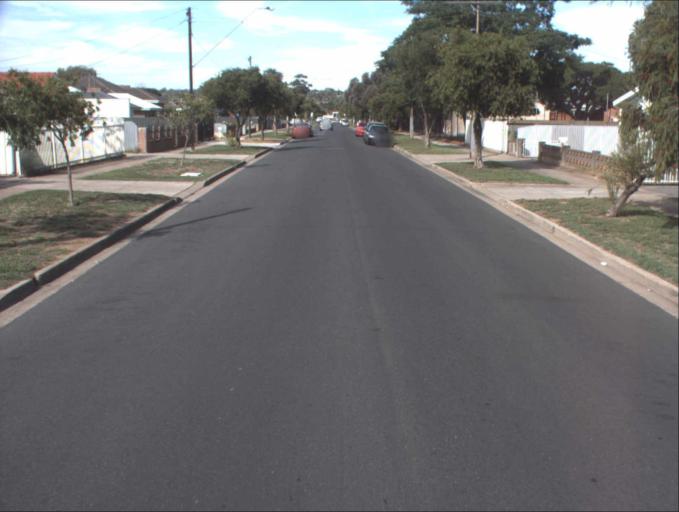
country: AU
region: South Australia
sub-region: Port Adelaide Enfield
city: Blair Athol
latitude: -34.8609
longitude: 138.5863
